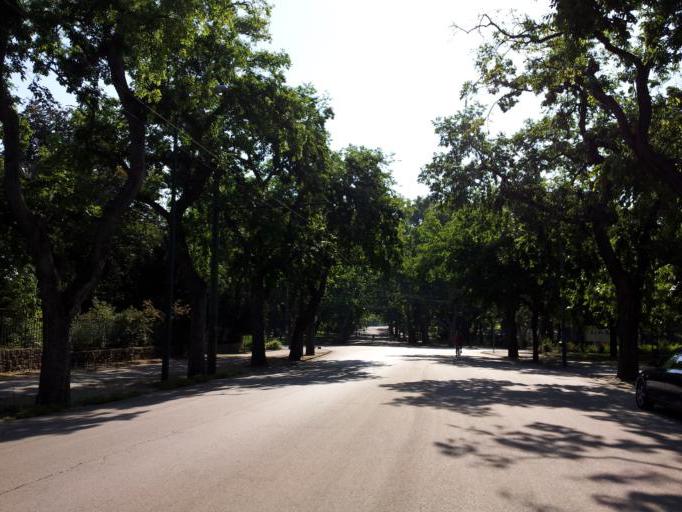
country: HU
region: Budapest
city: Budapest XIII. keruelet
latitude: 47.5124
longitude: 19.0830
